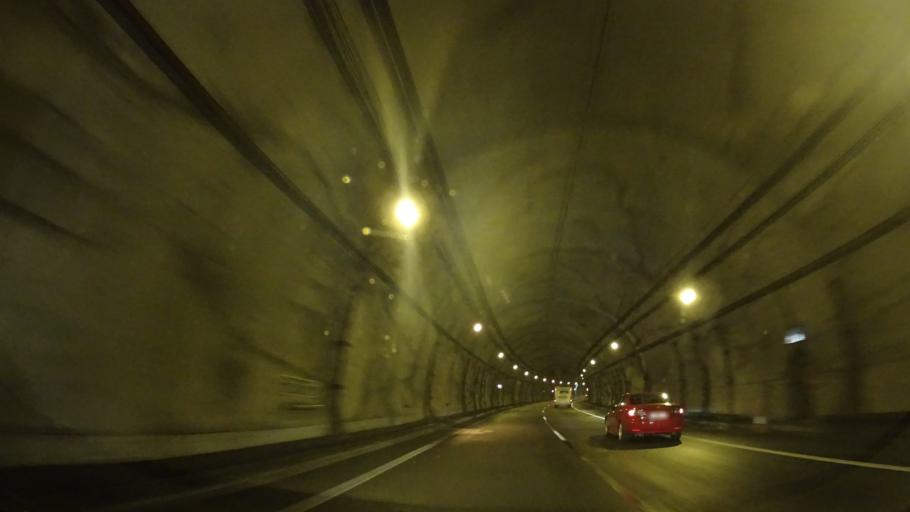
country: ES
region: Asturias
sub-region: Province of Asturias
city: Arriba
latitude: 43.4649
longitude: -5.5180
